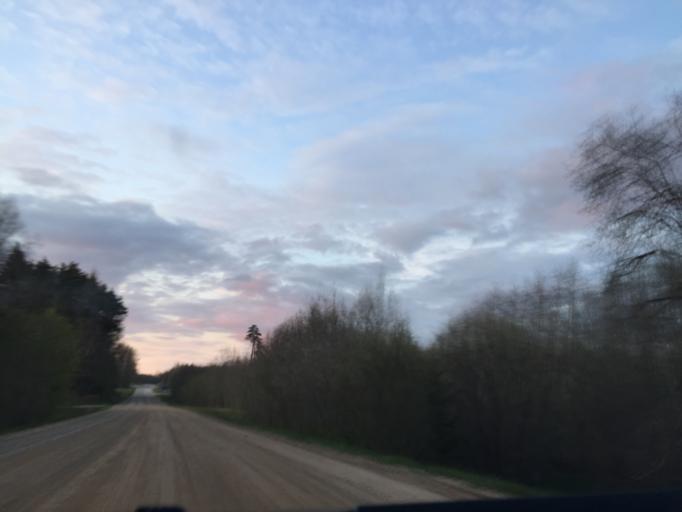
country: LV
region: Aluksnes Rajons
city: Aluksne
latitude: 57.3892
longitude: 27.0426
